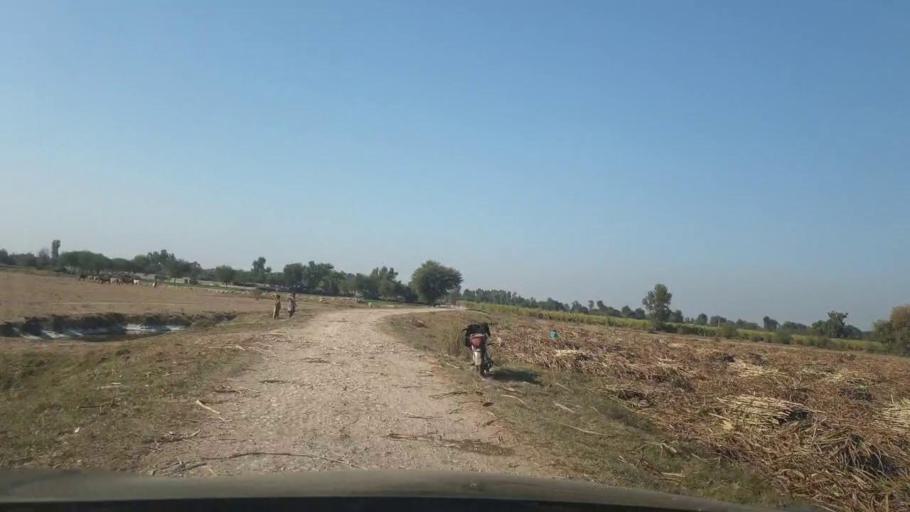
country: PK
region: Sindh
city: Mirpur Mathelo
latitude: 28.1448
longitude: 69.5927
